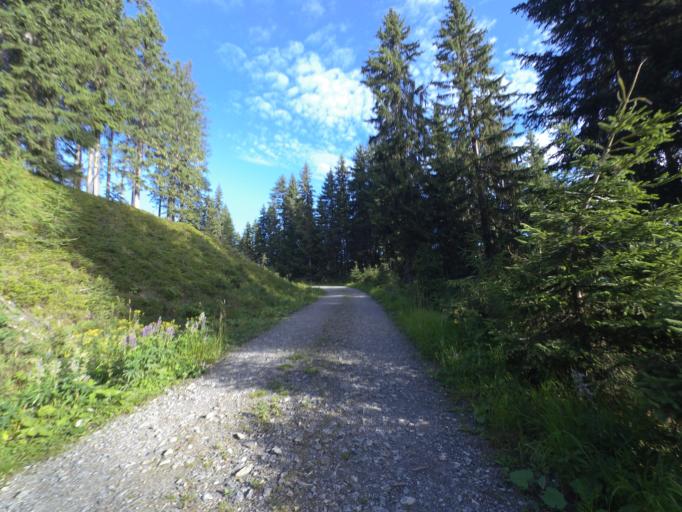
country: AT
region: Salzburg
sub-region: Politischer Bezirk Sankt Johann im Pongau
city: Goldegg
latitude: 47.3489
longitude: 13.0945
